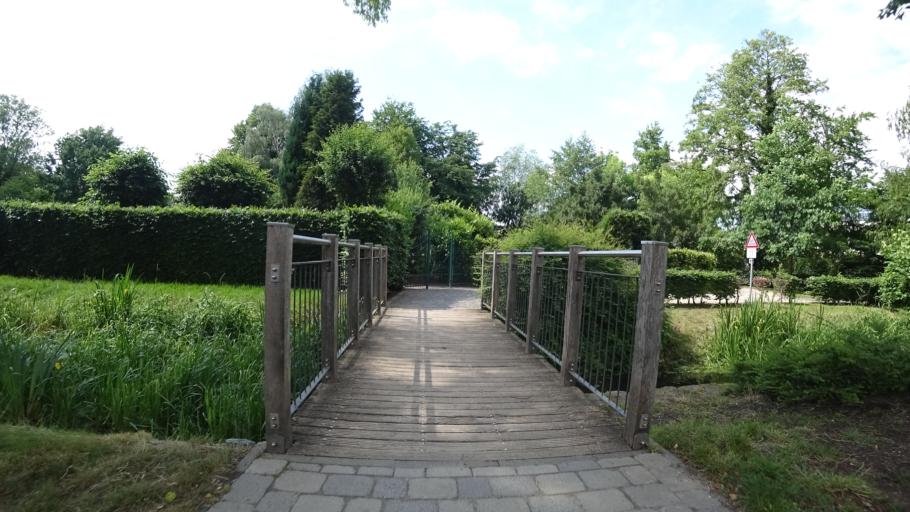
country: DE
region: North Rhine-Westphalia
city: Rietberg
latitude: 51.8099
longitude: 8.4261
